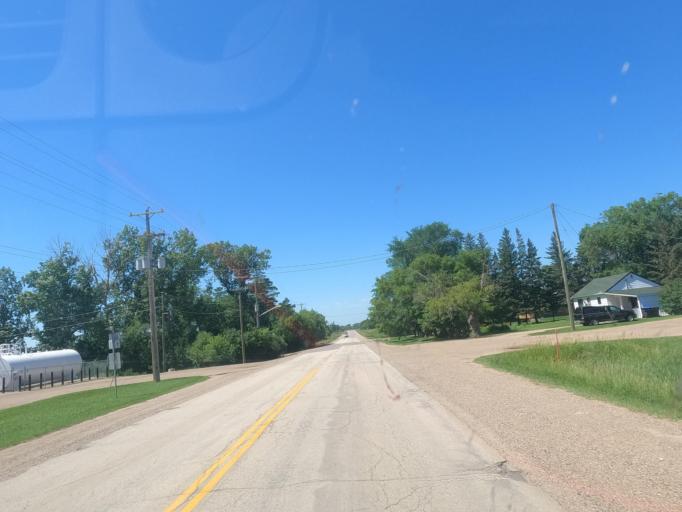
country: CA
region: Manitoba
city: Souris
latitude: 49.6211
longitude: -100.2726
